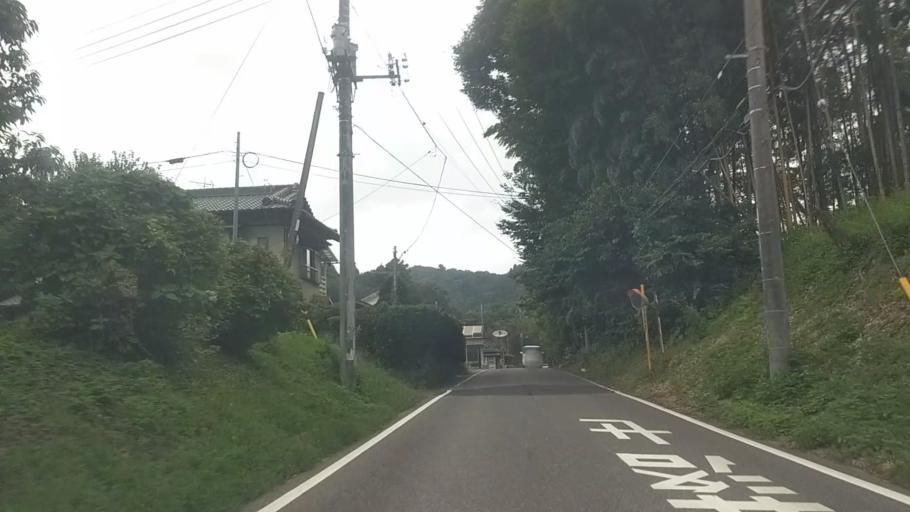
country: JP
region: Chiba
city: Kimitsu
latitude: 35.2295
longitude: 140.0112
